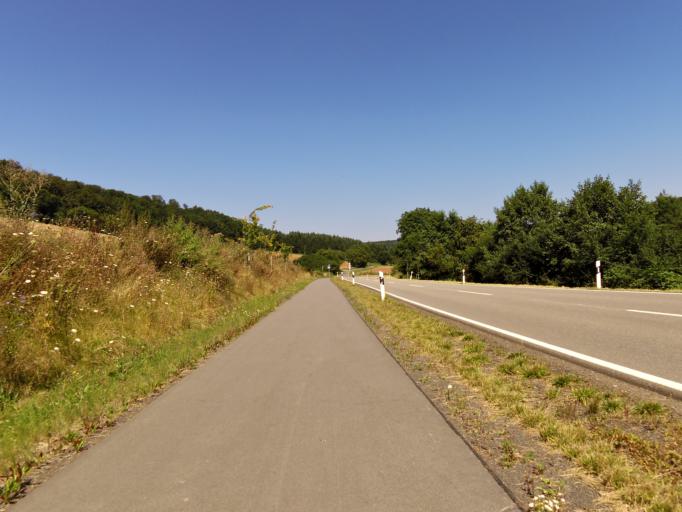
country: DE
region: Rheinland-Pfalz
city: Neuhemsbach
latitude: 49.5176
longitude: 7.8905
